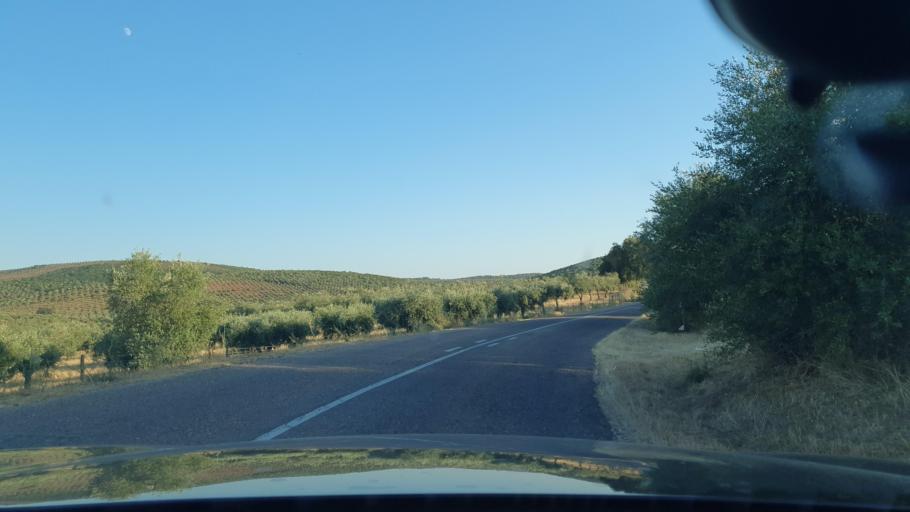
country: PT
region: Evora
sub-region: Estremoz
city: Estremoz
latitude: 38.9342
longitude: -7.6668
